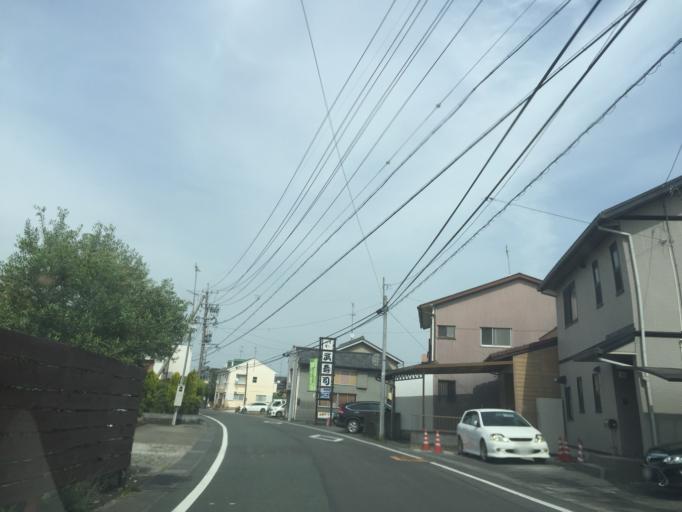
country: JP
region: Shizuoka
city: Kakegawa
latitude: 34.7725
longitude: 138.0225
